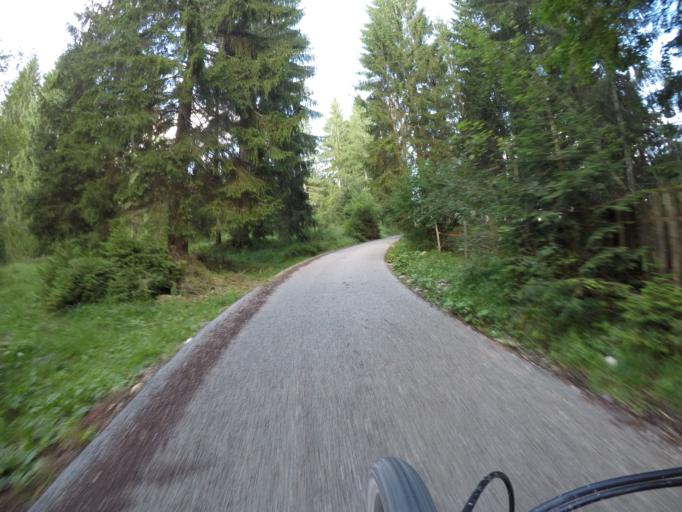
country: IT
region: Veneto
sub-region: Provincia di Vicenza
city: Gallio
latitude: 45.8866
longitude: 11.5293
